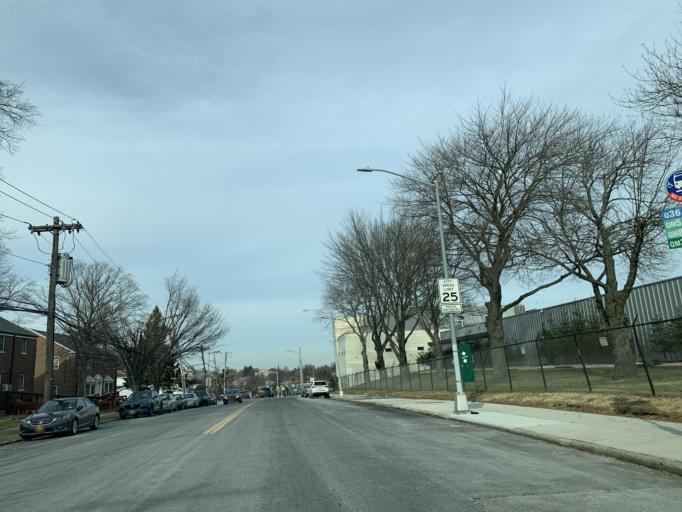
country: US
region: New York
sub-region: Nassau County
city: Lake Success
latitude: 40.7592
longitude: -73.7226
